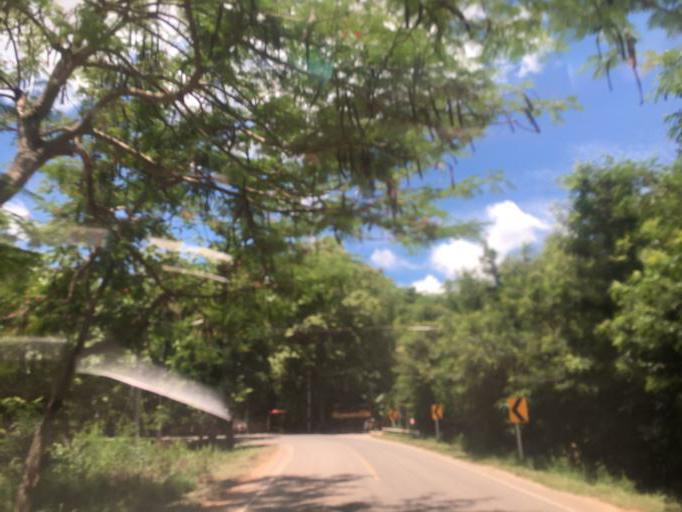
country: TH
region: Changwat Udon Thani
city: Nong Saeng
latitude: 17.2079
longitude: 102.7494
